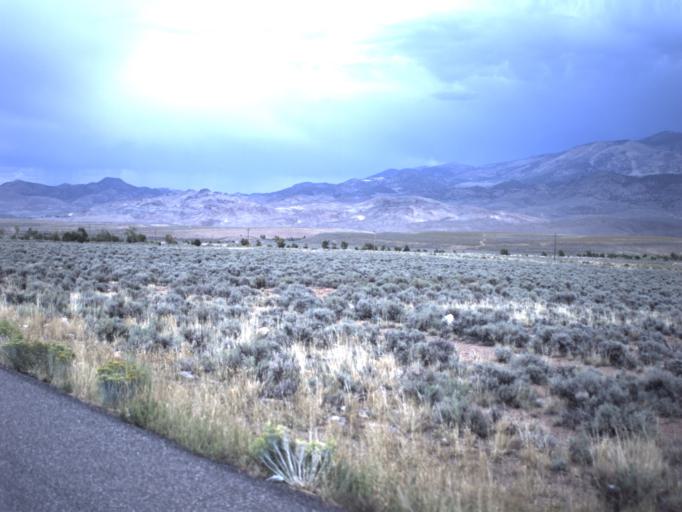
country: US
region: Utah
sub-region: Piute County
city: Junction
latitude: 38.3856
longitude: -112.2294
